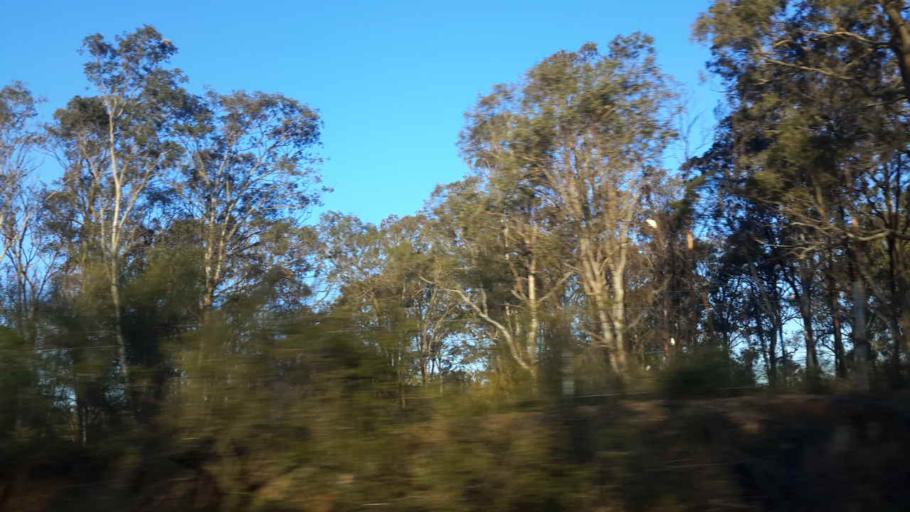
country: AU
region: New South Wales
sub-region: Wollondilly
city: Douglas Park
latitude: -34.2297
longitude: 150.7279
